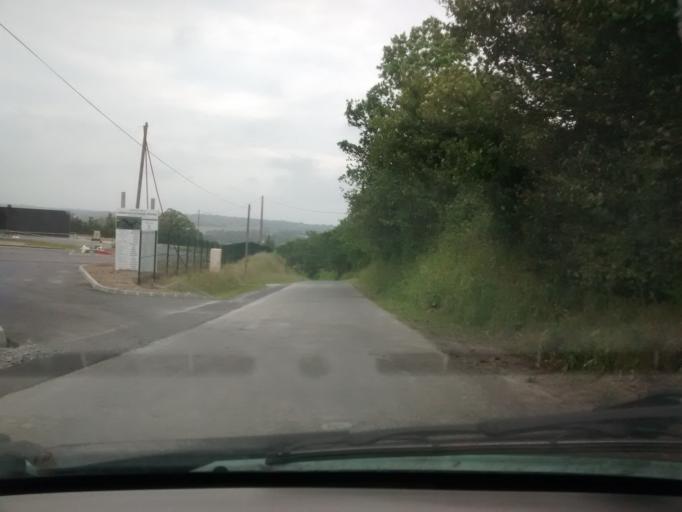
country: FR
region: Lower Normandy
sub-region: Departement de la Manche
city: Saint-Lo
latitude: 49.0987
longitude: -1.0674
